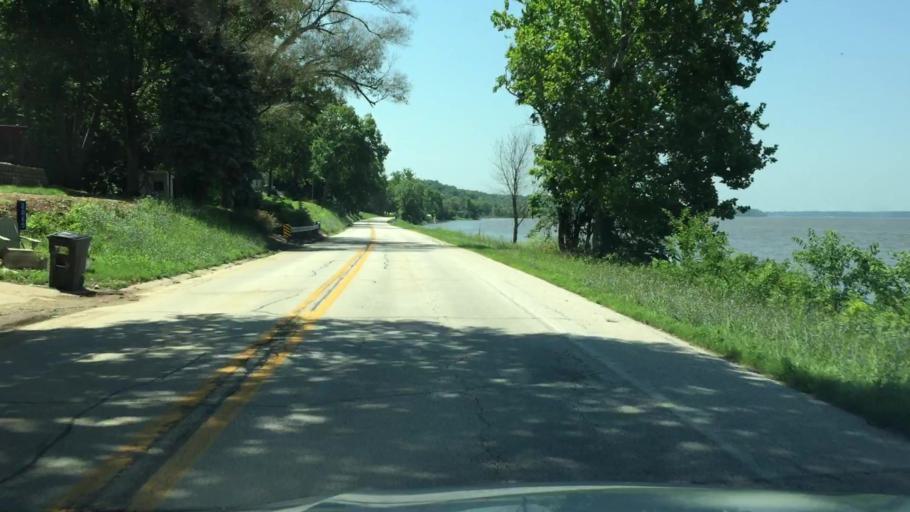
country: US
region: Illinois
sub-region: Hancock County
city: Nauvoo
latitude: 40.5037
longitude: -91.3564
